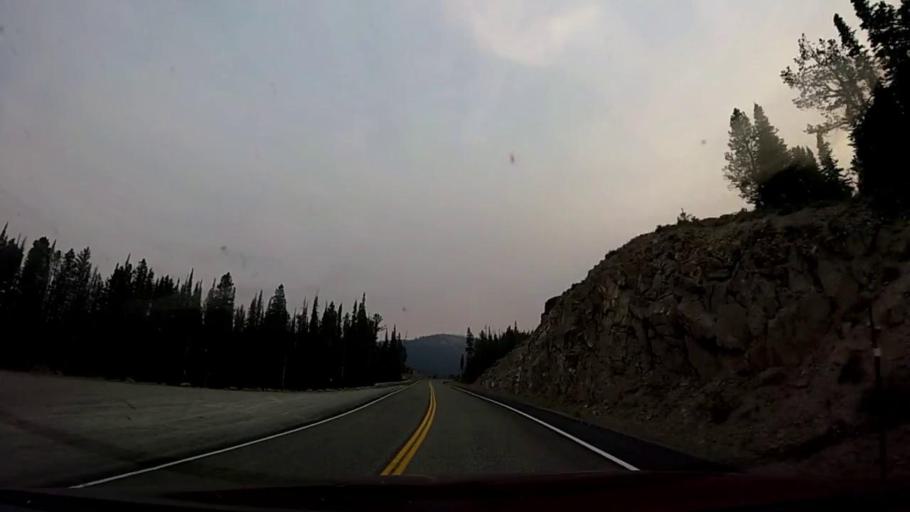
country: US
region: Idaho
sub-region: Blaine County
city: Ketchum
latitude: 43.8760
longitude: -114.7050
